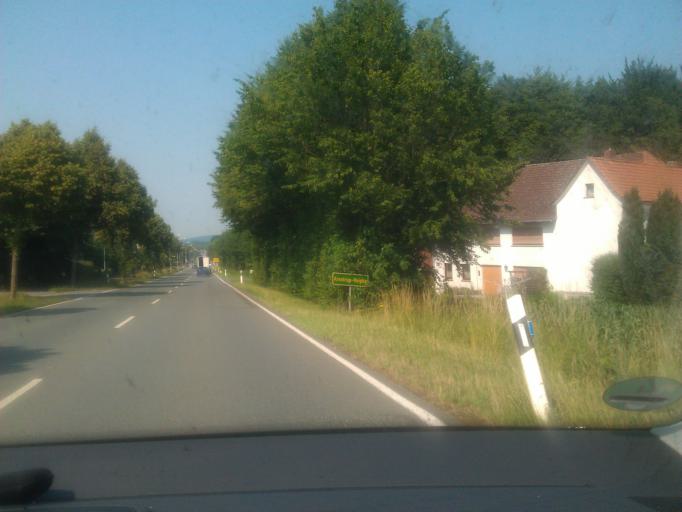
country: DE
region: North Rhine-Westphalia
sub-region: Regierungsbezirk Detmold
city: Leopoldshohe
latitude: 52.0231
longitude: 8.7136
